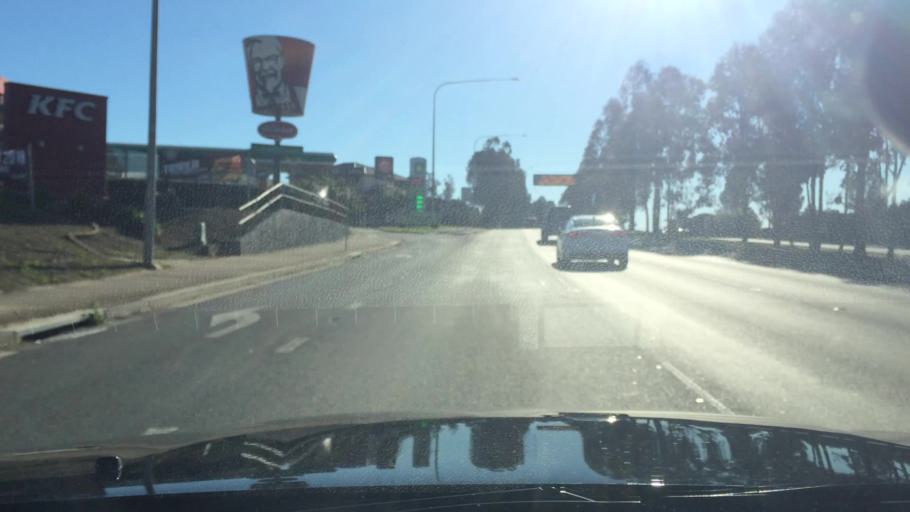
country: AU
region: New South Wales
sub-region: Liverpool
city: Miller
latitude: -33.9237
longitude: 150.8487
